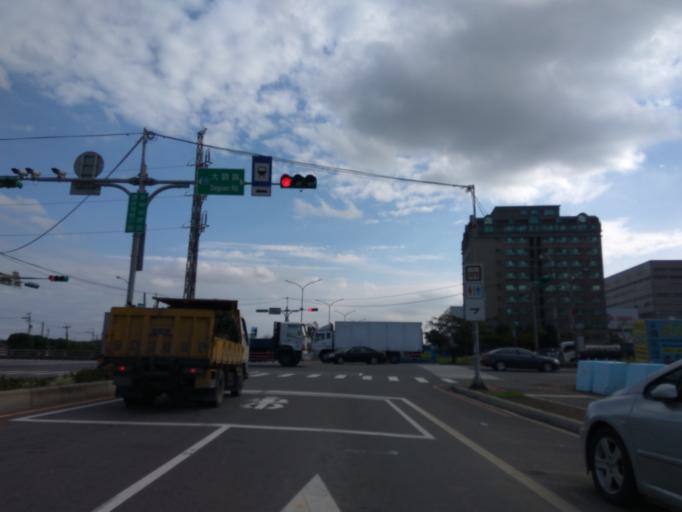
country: TW
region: Taiwan
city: Taoyuan City
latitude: 25.0632
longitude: 121.1771
